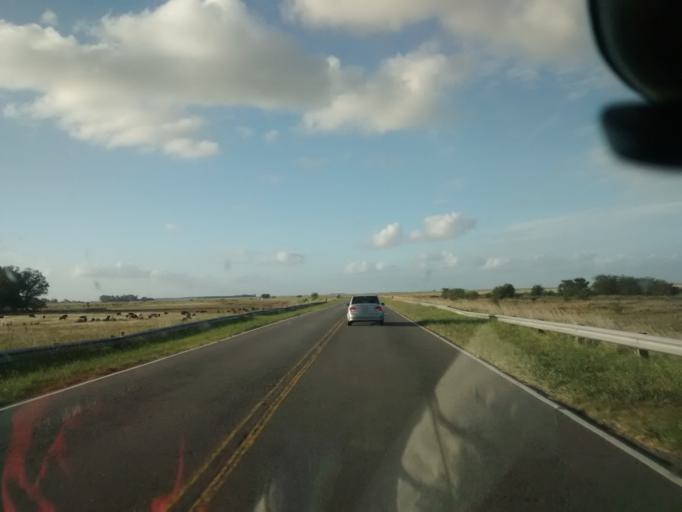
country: AR
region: Buenos Aires
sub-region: Partido de General Belgrano
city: General Belgrano
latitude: -36.1309
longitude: -58.5931
